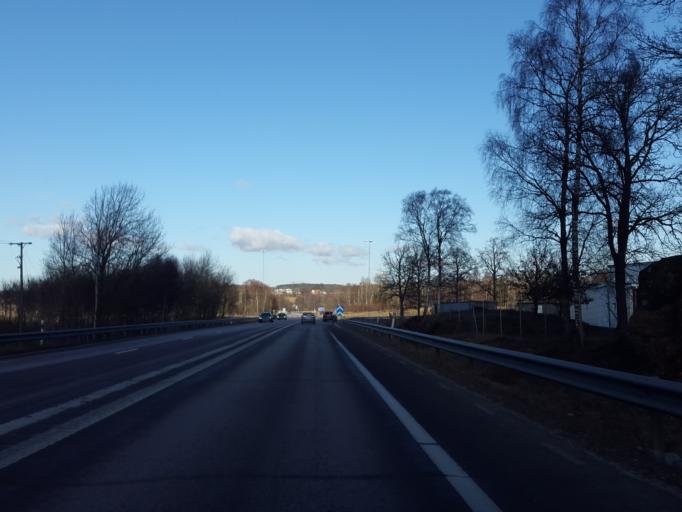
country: SE
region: Vaestra Goetaland
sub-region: Vargarda Kommun
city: Vargarda
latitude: 58.0212
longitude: 12.7811
